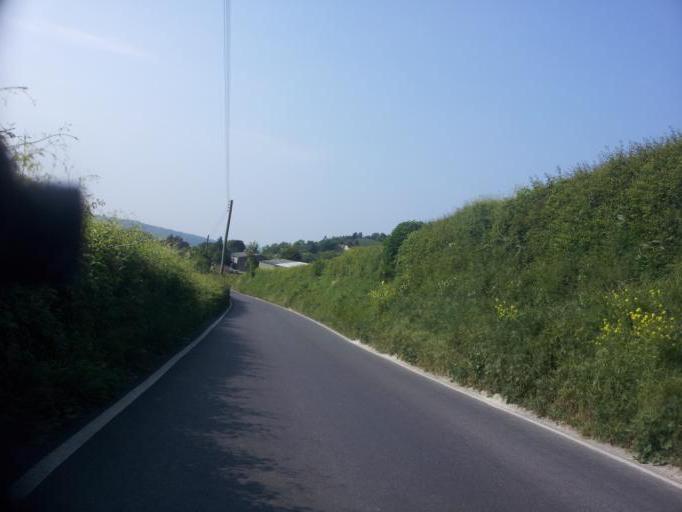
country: GB
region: England
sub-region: Medway
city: Halling
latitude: 51.3378
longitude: 0.4729
